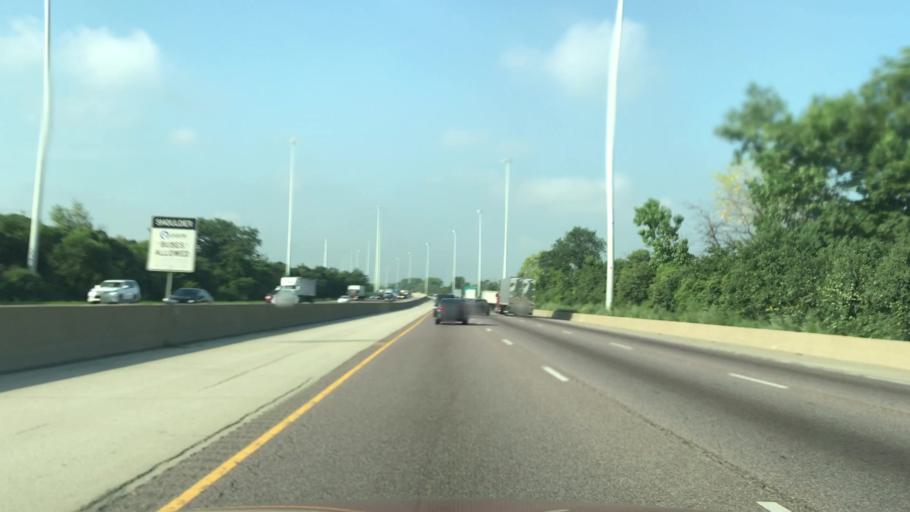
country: US
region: Illinois
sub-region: Cook County
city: Hodgkins
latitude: 41.7761
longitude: -87.8403
